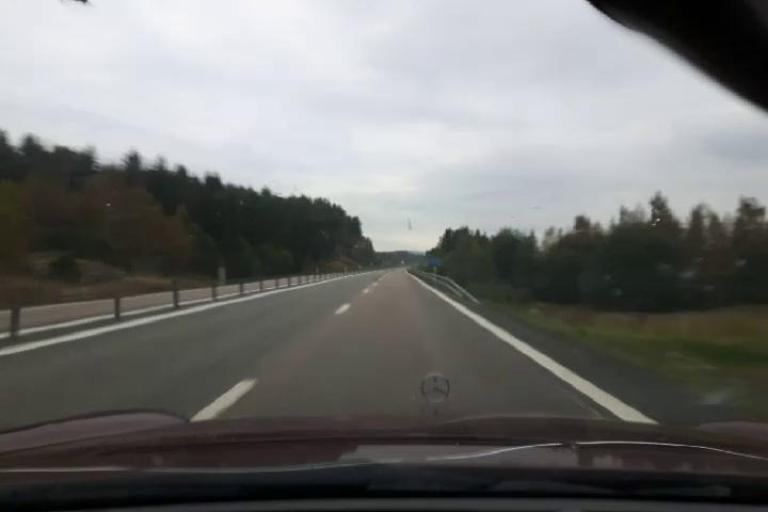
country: SE
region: Vaesternorrland
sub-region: Kramfors Kommun
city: Nordingra
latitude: 62.9266
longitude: 18.0982
